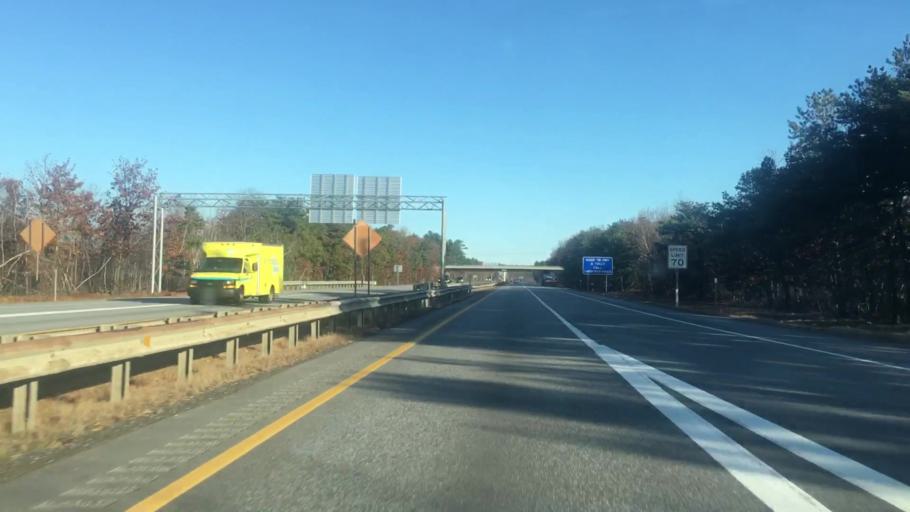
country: US
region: Maine
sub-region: Cumberland County
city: New Gloucester
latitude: 43.9384
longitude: -70.3344
